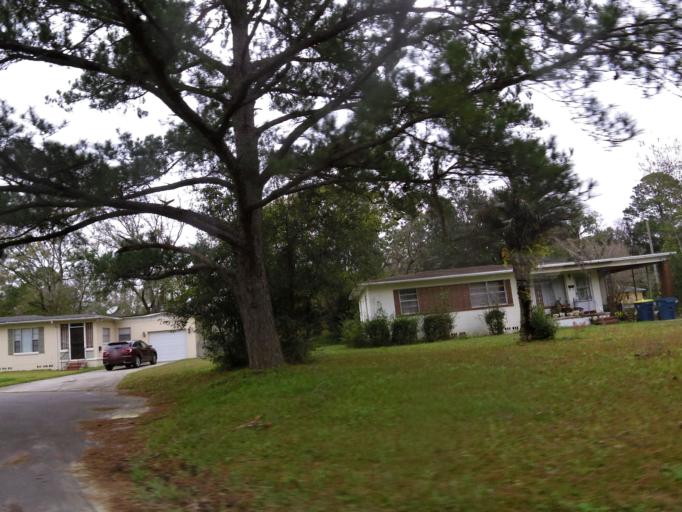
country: US
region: Florida
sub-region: Duval County
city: Jacksonville
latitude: 30.3732
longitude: -81.7048
